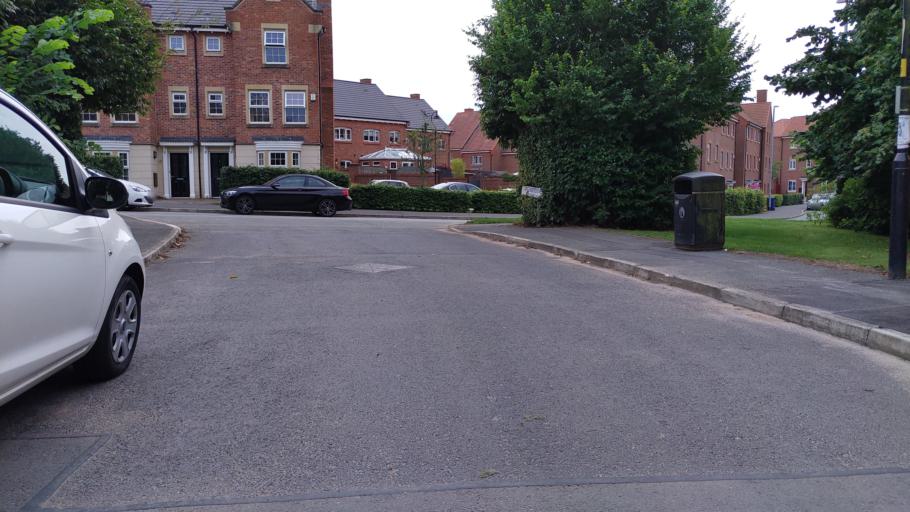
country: GB
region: England
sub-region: Lancashire
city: Coppull
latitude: 53.6314
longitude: -2.6386
